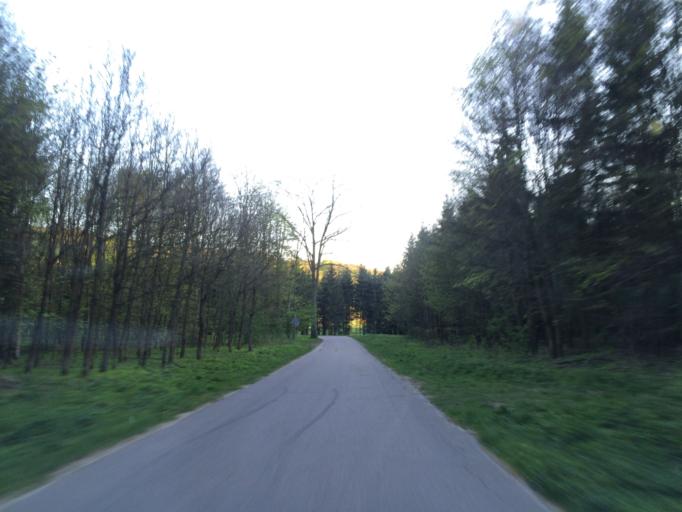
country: PL
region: Warmian-Masurian Voivodeship
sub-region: Powiat ilawski
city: Lubawa
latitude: 53.5116
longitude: 19.8723
